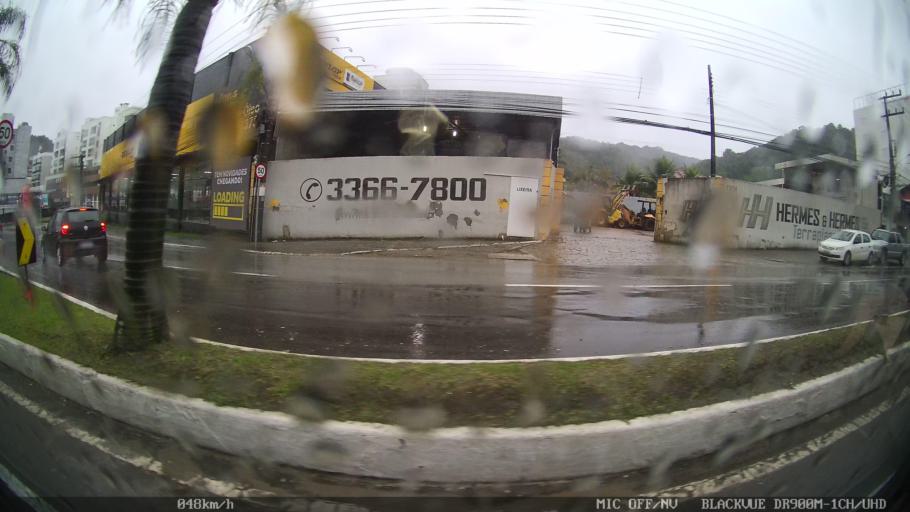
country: BR
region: Santa Catarina
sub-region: Balneario Camboriu
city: Balneario Camboriu
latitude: -26.9664
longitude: -48.6396
